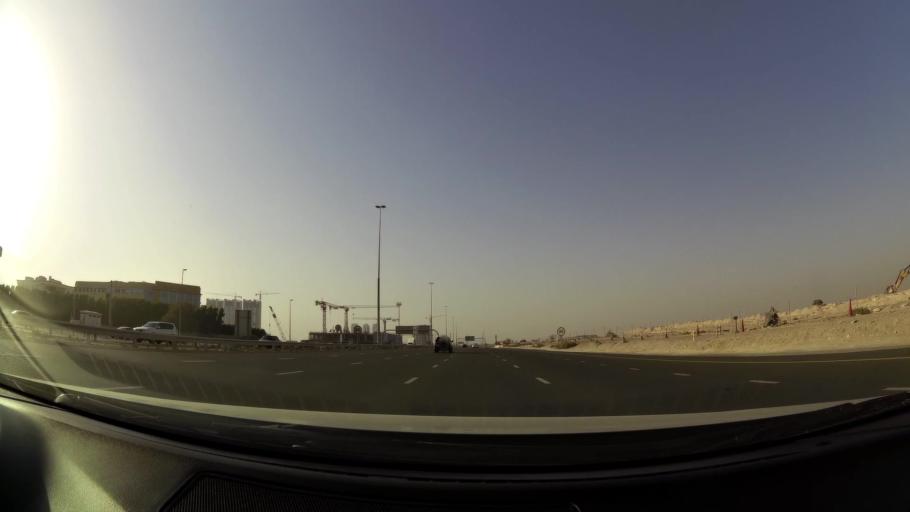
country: AE
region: Dubai
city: Dubai
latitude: 25.0623
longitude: 55.2498
